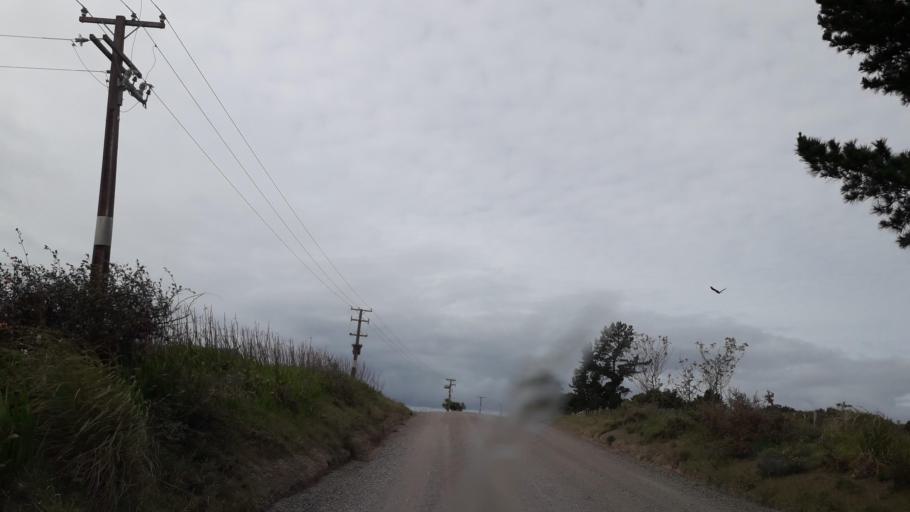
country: NZ
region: Northland
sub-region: Far North District
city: Kerikeri
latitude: -35.1341
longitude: 173.9993
